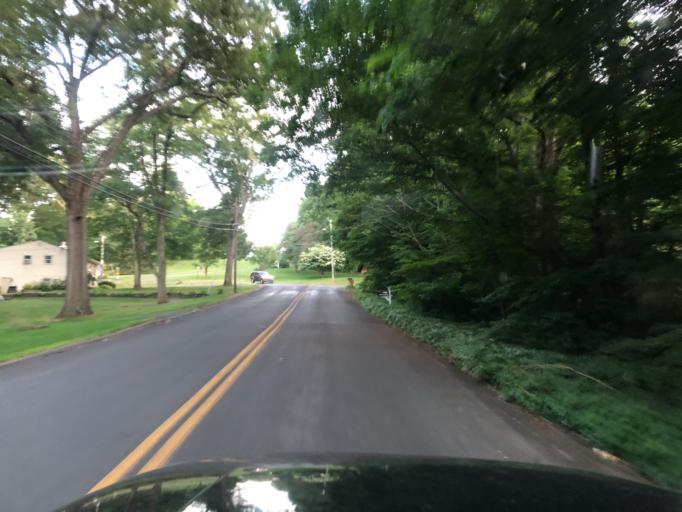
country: US
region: Connecticut
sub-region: Middlesex County
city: Durham
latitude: 41.5334
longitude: -72.7018
